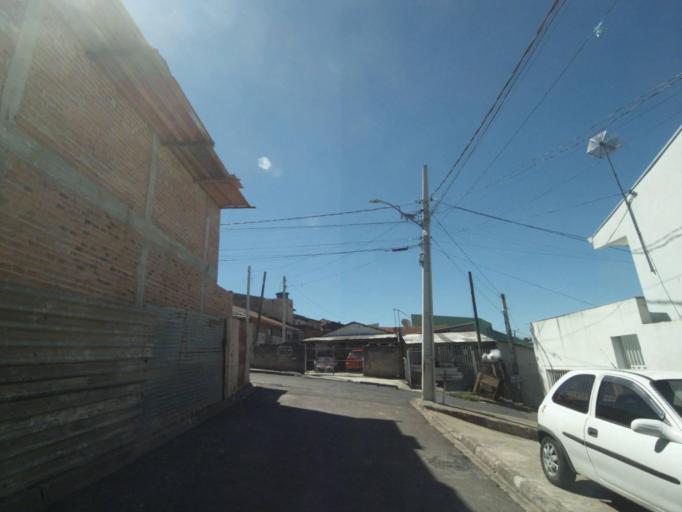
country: BR
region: Parana
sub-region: Curitiba
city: Curitiba
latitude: -25.4619
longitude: -49.3407
